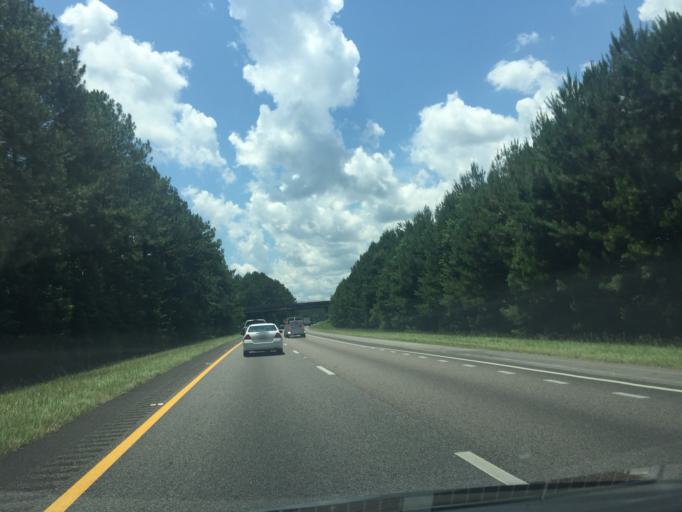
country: US
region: South Carolina
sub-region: Jasper County
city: Hardeeville
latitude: 32.2551
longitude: -81.1040
